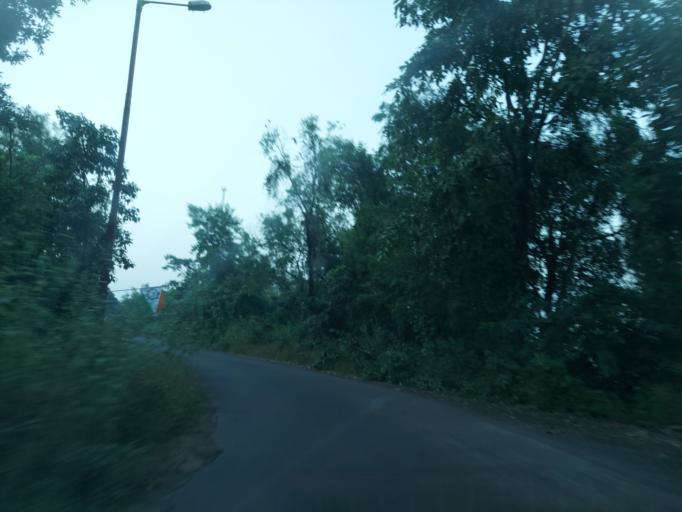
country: IN
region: Maharashtra
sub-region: Sindhudurg
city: Kudal
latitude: 16.1131
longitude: 73.7001
